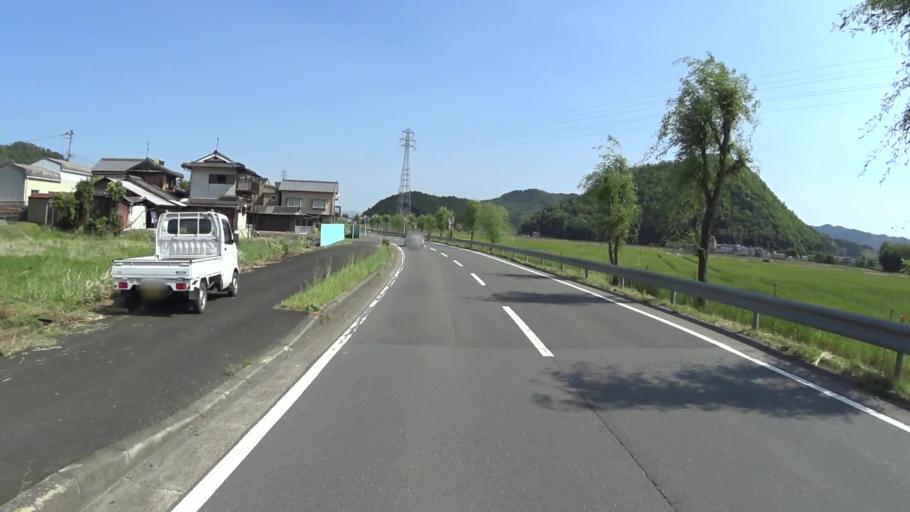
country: JP
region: Kyoto
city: Kameoka
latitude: 35.1103
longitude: 135.5198
